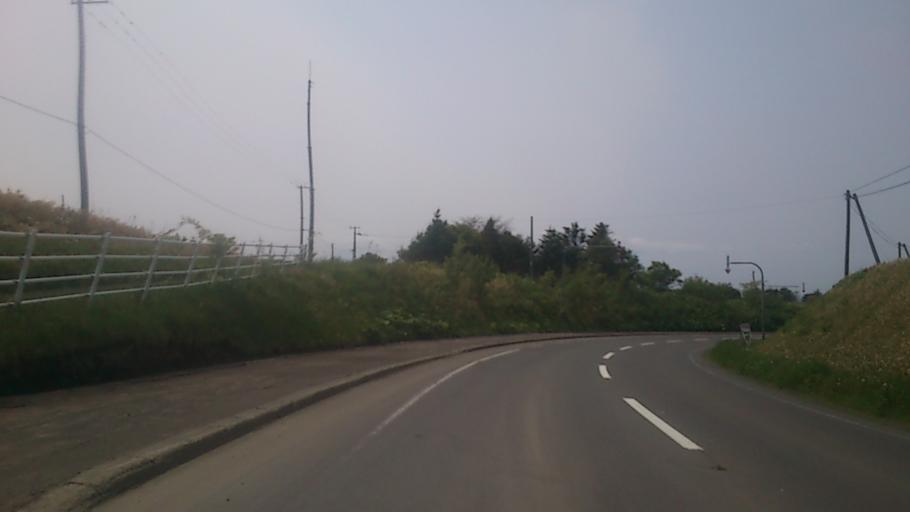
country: JP
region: Hokkaido
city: Nemuro
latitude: 43.2787
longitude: 145.5106
